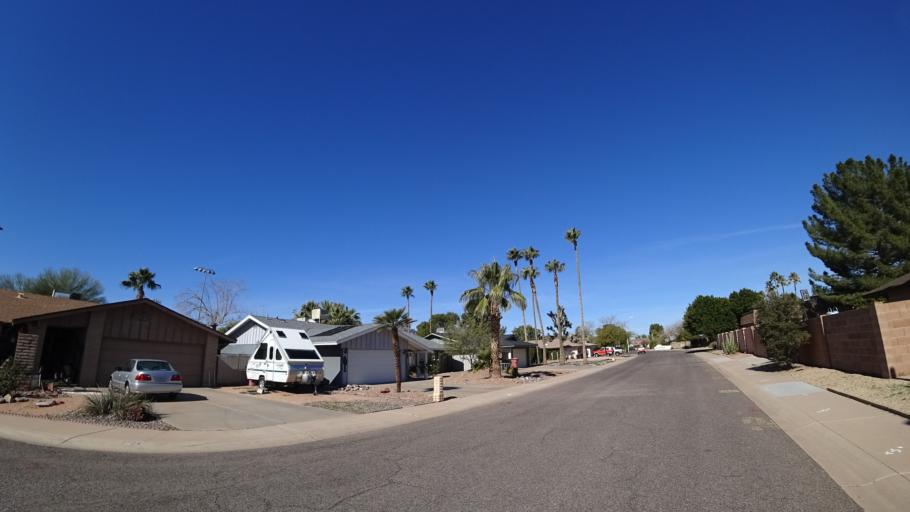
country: US
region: Arizona
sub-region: Maricopa County
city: Scottsdale
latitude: 33.5196
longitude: -111.9057
